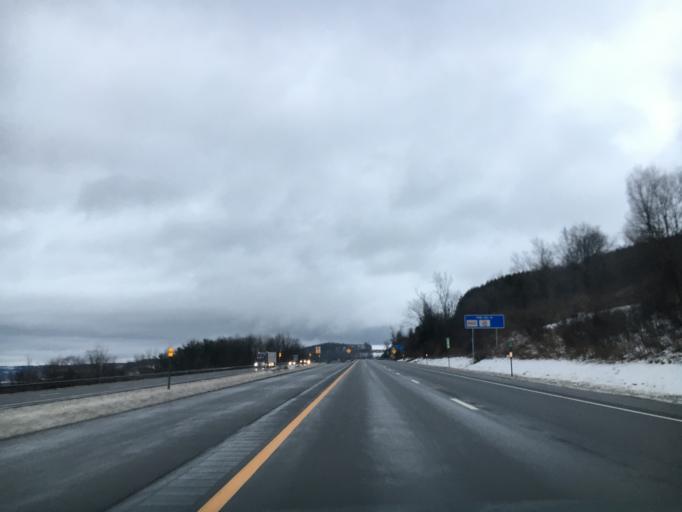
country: US
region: New York
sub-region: Cortland County
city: McGraw
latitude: 42.5768
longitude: -76.1219
